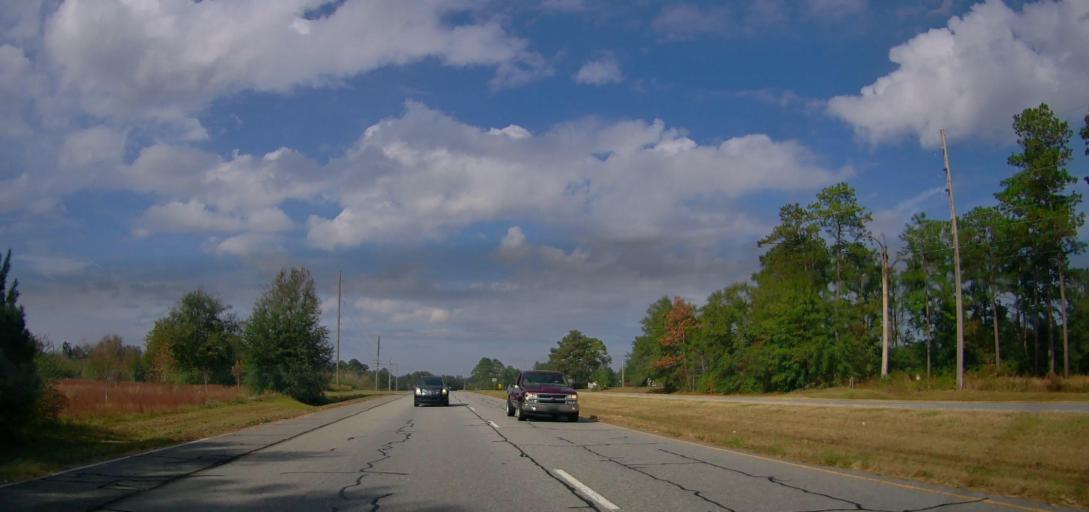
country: US
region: Georgia
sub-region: Mitchell County
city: Pelham
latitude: 31.1691
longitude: -84.1461
